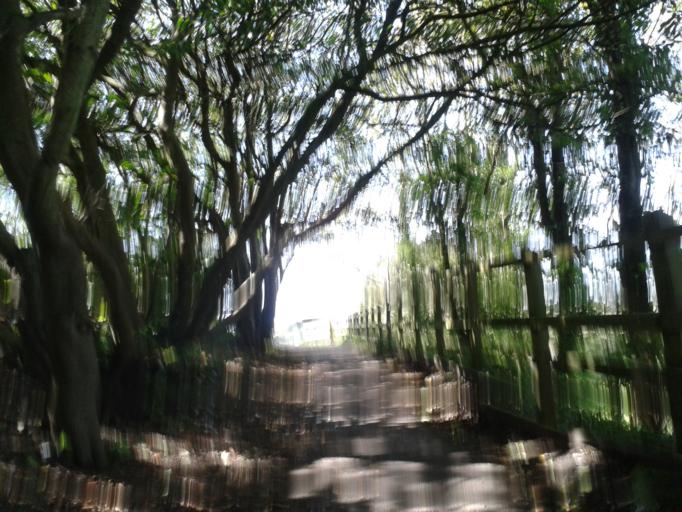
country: GB
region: England
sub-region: Devon
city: Barnstaple
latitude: 51.0684
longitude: -4.0553
